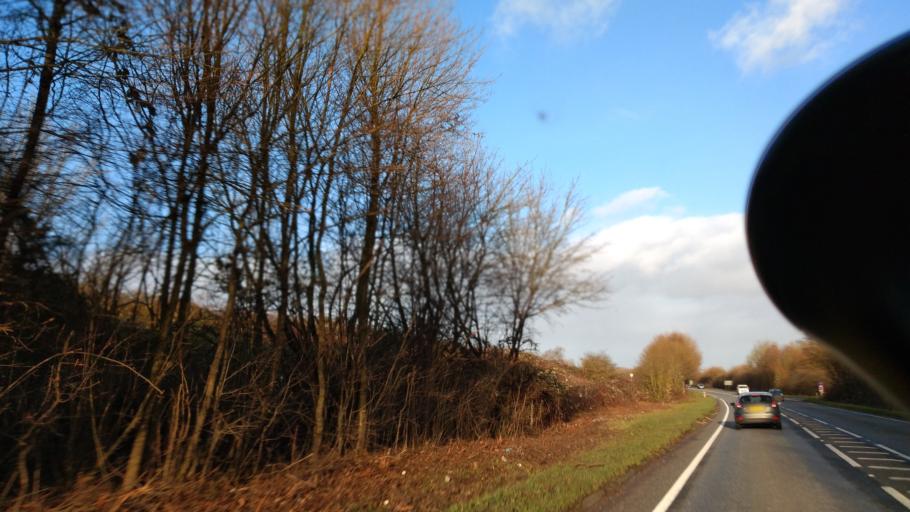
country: GB
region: England
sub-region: Somerset
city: Frome
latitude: 51.2153
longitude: -2.3077
